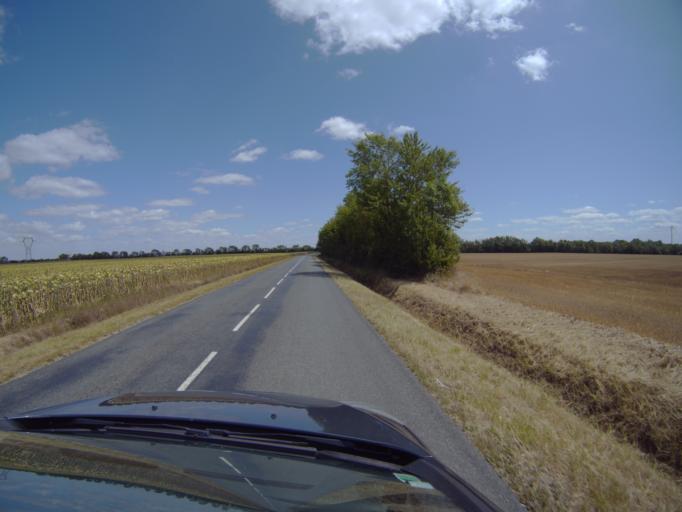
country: FR
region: Poitou-Charentes
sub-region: Departement de la Charente-Maritime
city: Courcon
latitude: 46.2550
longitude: -0.8417
